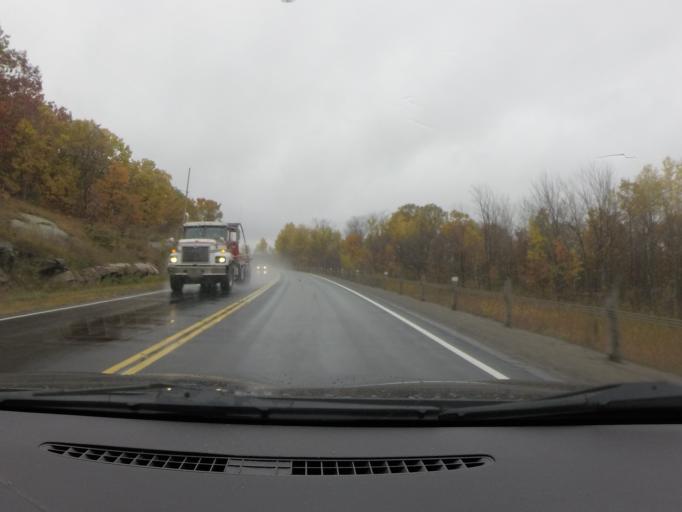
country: CA
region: Ontario
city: Deseronto
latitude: 44.5976
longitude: -77.1886
